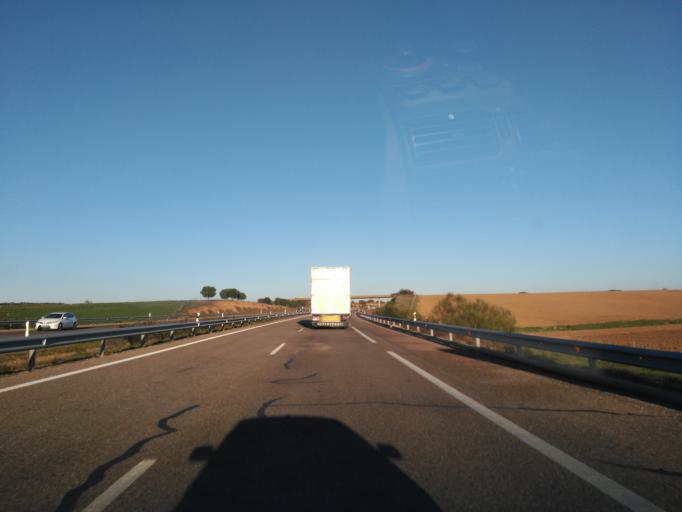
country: ES
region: Castille and Leon
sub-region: Provincia de Salamanca
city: Parada de Rubiales
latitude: 41.1614
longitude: -5.4423
